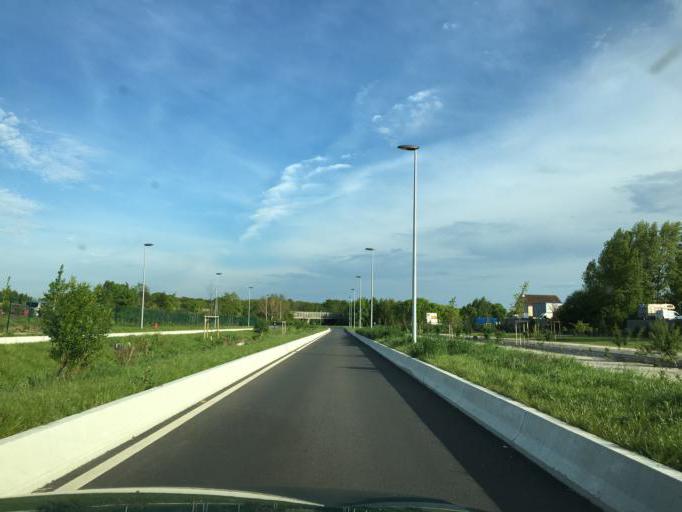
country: FR
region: Centre
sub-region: Departement du Loiret
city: Ingre
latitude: 47.9301
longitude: 1.8468
